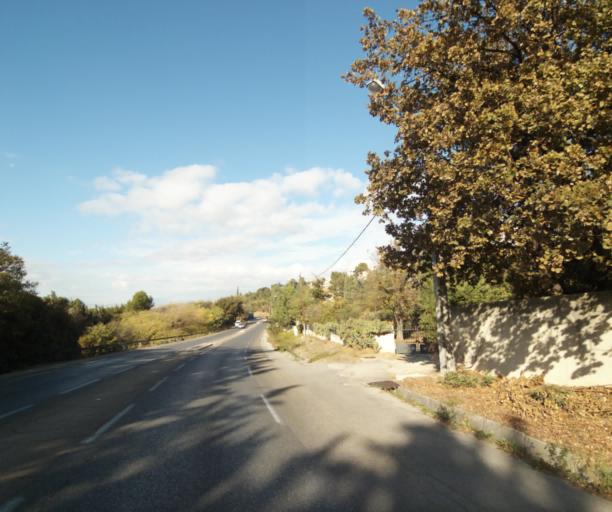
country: FR
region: Provence-Alpes-Cote d'Azur
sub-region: Departement des Bouches-du-Rhone
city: Allauch
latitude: 43.3323
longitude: 5.4844
